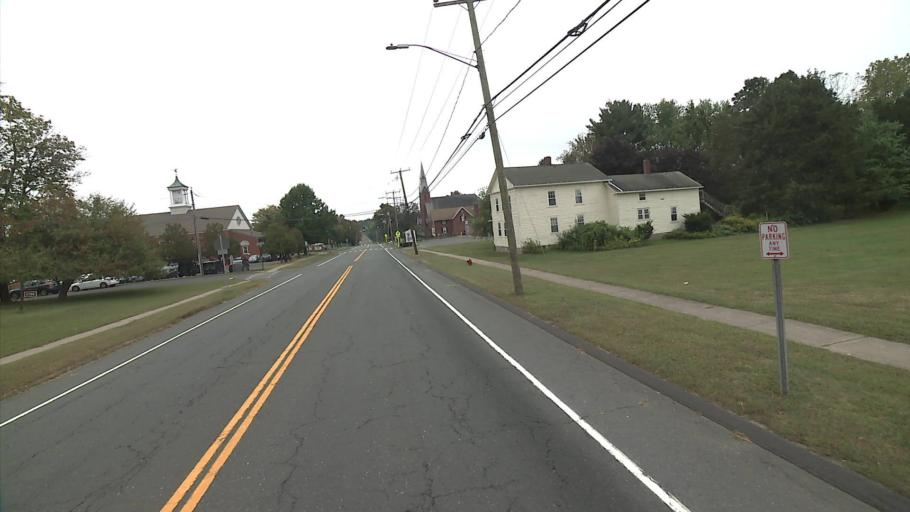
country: US
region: Connecticut
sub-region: Hartford County
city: Windsor Locks
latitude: 41.9053
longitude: -72.6792
